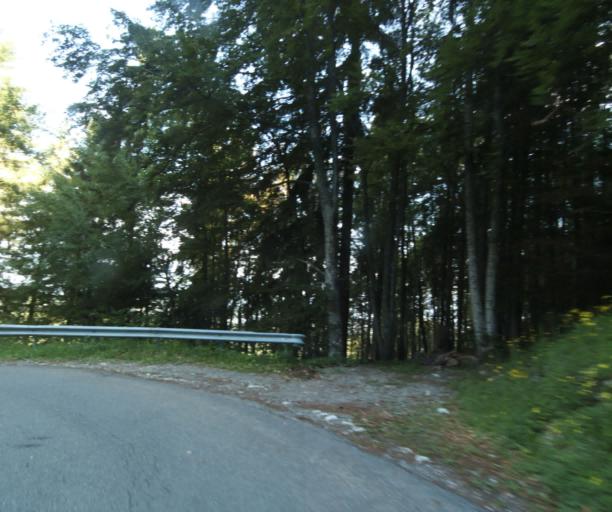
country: FR
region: Rhone-Alpes
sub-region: Departement de la Haute-Savoie
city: Lyaud
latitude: 46.3023
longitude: 6.5081
